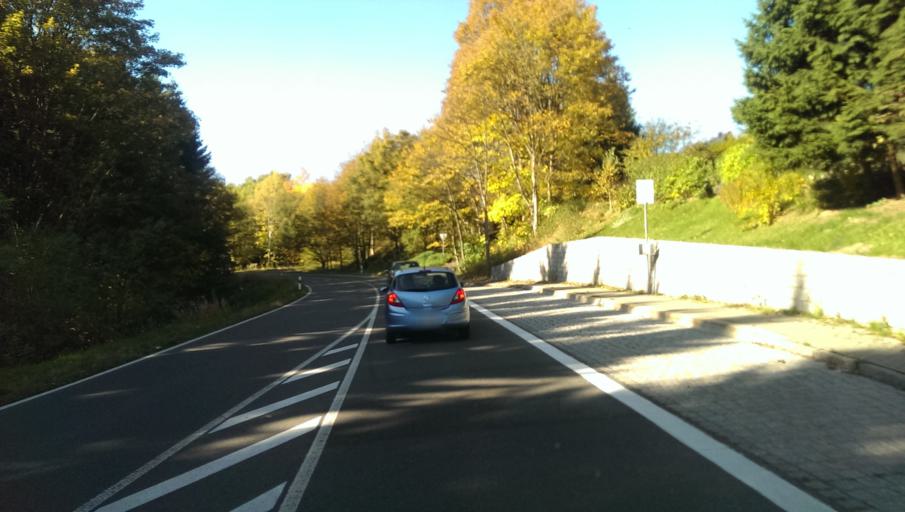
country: DE
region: Saxony
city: Geising
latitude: 50.7620
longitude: 13.7722
